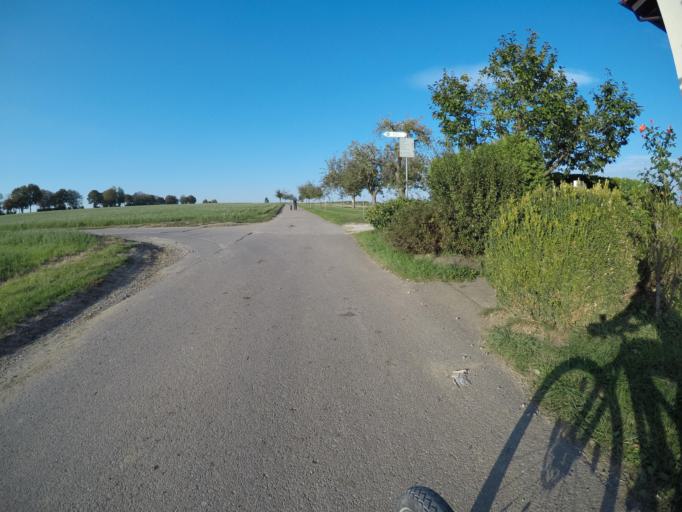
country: DE
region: Baden-Wuerttemberg
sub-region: Regierungsbezirk Stuttgart
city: Ostfildern
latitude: 48.7285
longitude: 9.2370
